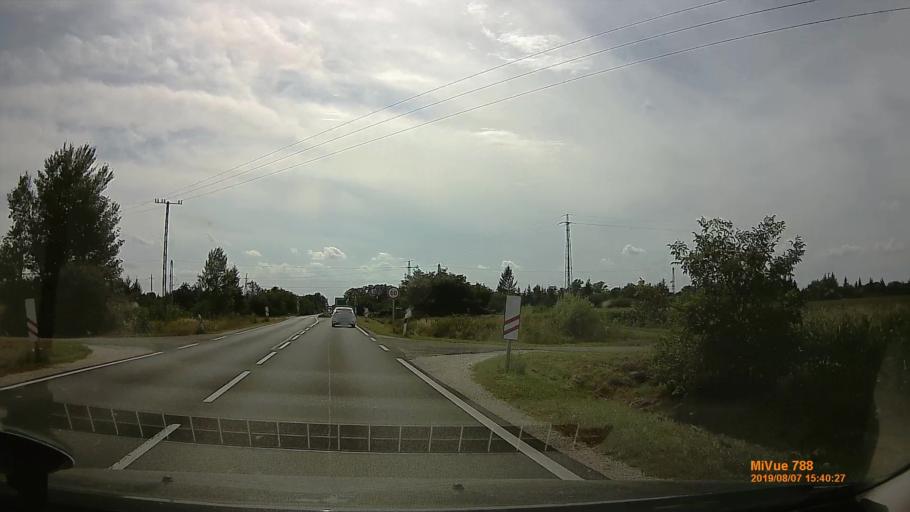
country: HU
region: Vas
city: Szombathely
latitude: 47.2140
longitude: 16.6488
